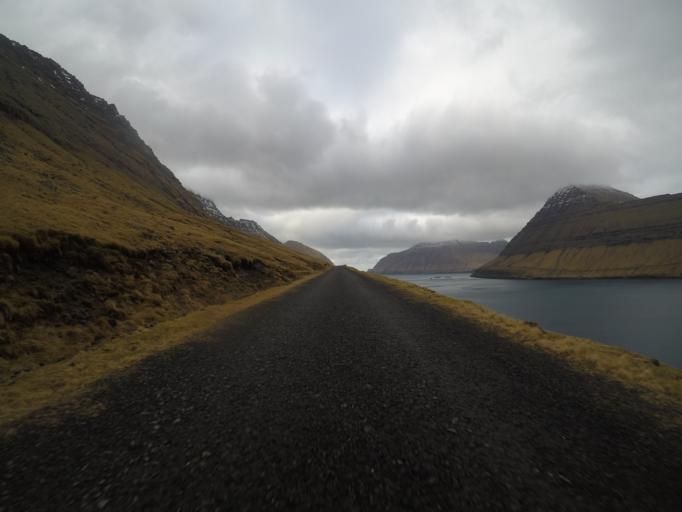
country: FO
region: Nordoyar
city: Klaksvik
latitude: 62.3217
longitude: -6.5606
